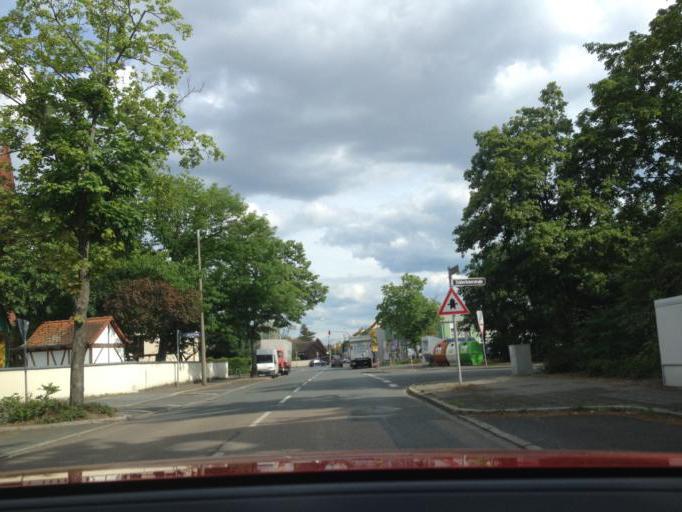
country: DE
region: Bavaria
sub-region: Regierungsbezirk Mittelfranken
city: Grossreuth bei Schweinau
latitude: 49.4560
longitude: 11.0154
